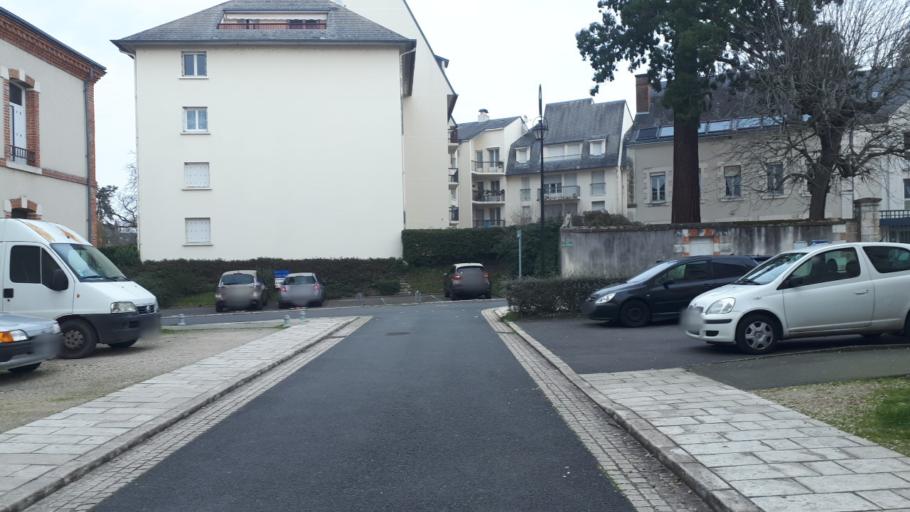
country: FR
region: Centre
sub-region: Departement du Loir-et-Cher
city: Romorantin-Lanthenay
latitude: 47.3560
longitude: 1.7452
